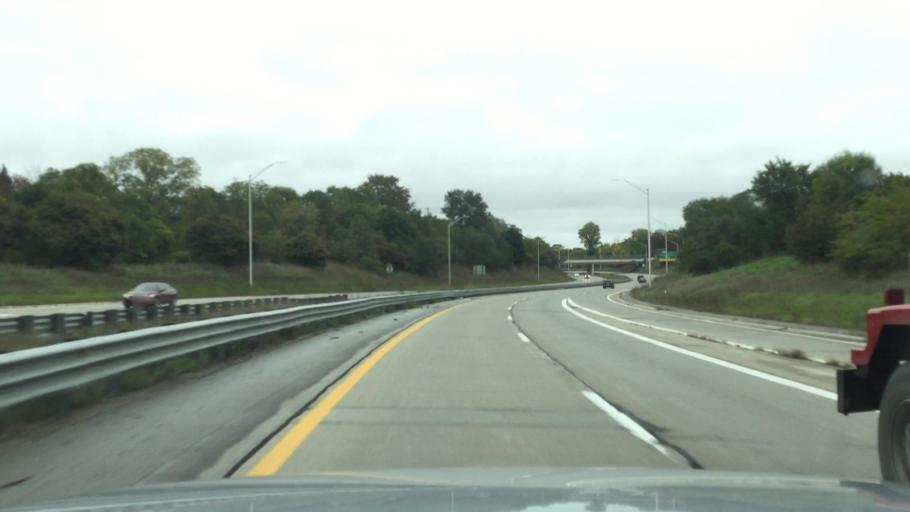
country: US
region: Michigan
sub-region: Saginaw County
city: Carrollton
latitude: 43.4357
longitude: -83.9230
